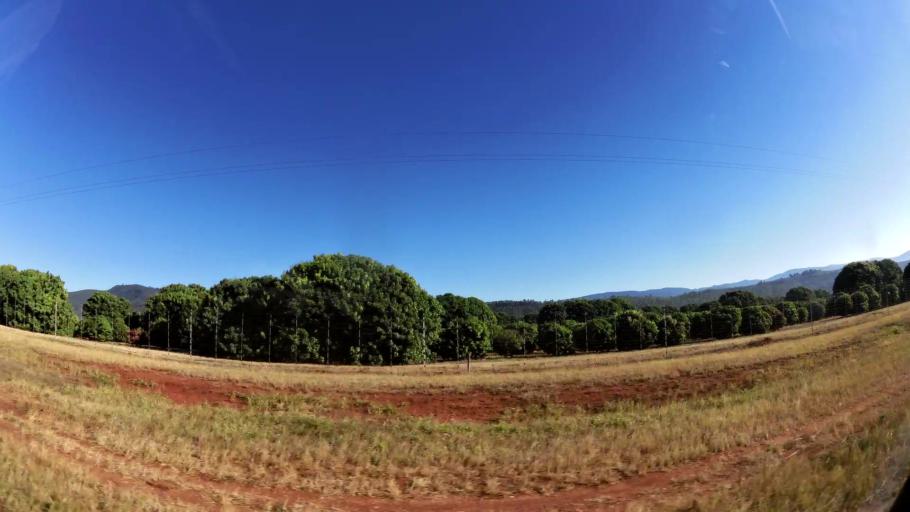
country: ZA
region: Limpopo
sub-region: Mopani District Municipality
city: Tzaneen
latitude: -23.8515
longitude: 30.1160
